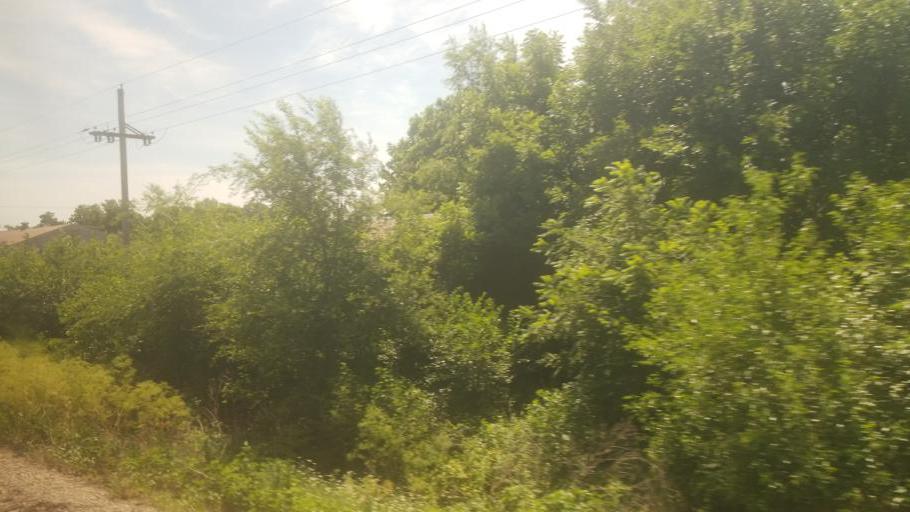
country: US
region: Missouri
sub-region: Carroll County
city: Carrollton
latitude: 39.3011
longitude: -93.6883
